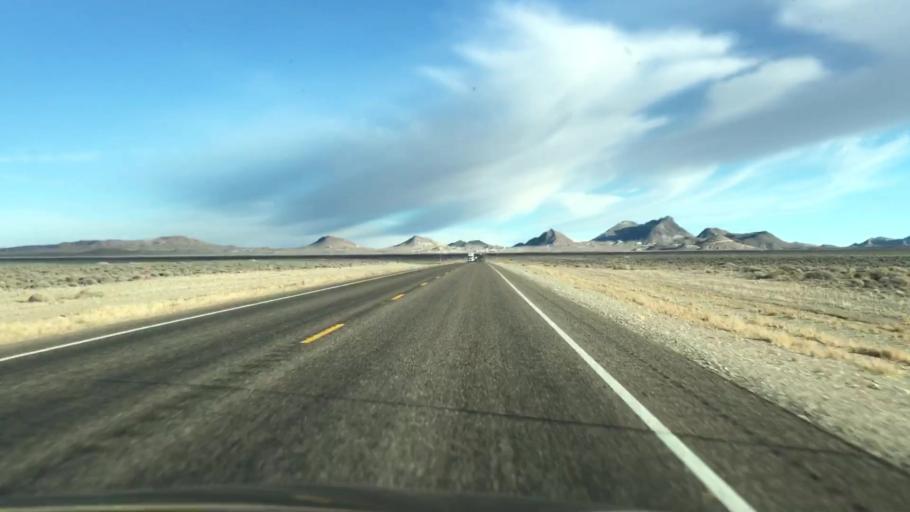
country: US
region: Nevada
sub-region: Nye County
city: Tonopah
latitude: 38.0994
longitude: -117.3264
